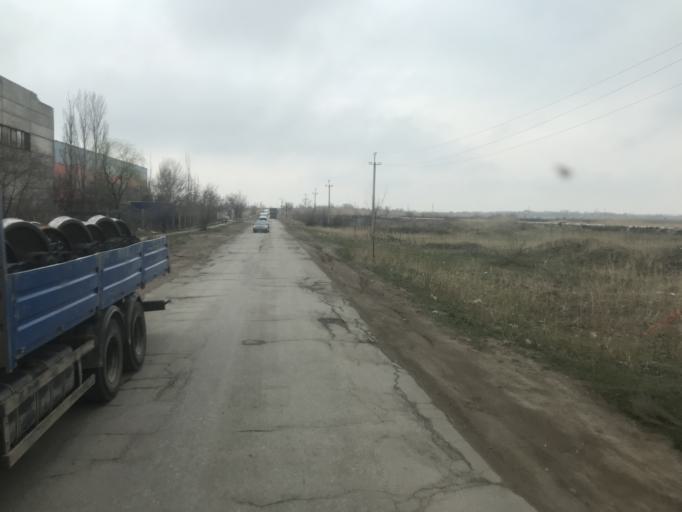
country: RU
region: Volgograd
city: Svetlyy Yar
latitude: 48.5260
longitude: 44.6148
